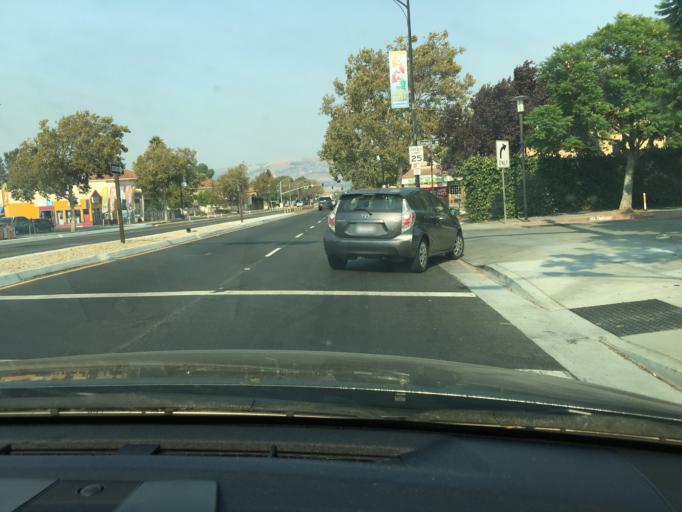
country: US
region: California
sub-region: Santa Clara County
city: Alum Rock
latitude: 37.3534
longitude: -121.8540
